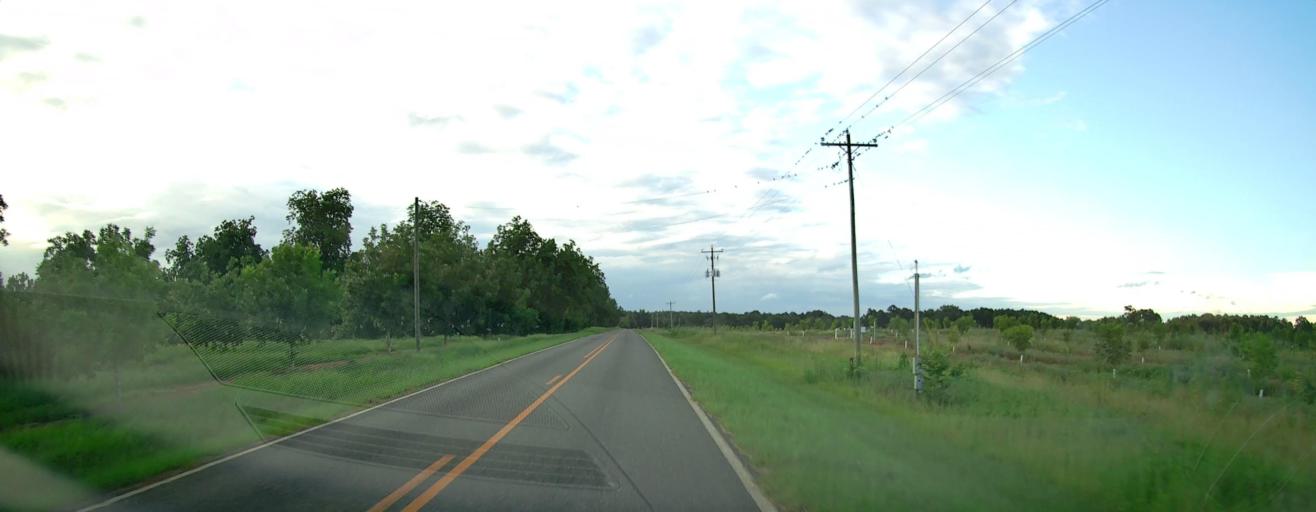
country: US
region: Georgia
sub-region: Pulaski County
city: Hawkinsville
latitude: 32.3170
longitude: -83.5522
